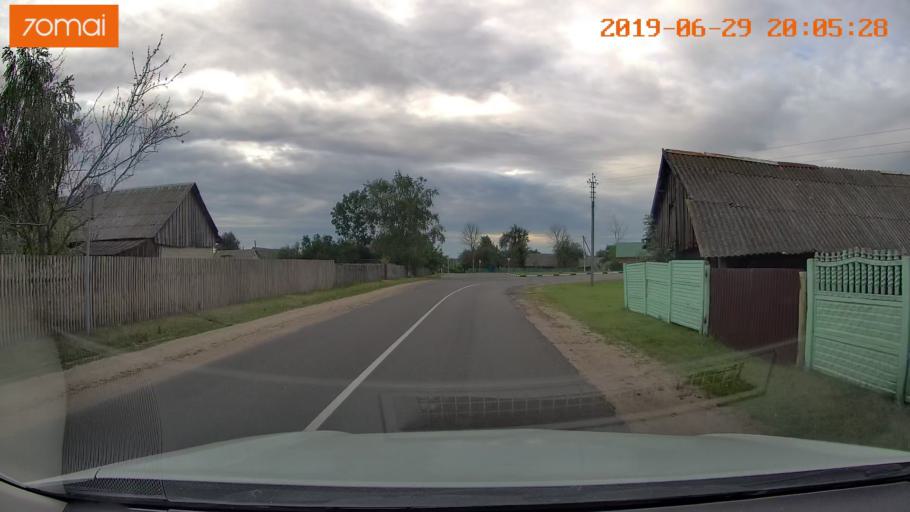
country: BY
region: Brest
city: Lahishyn
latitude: 52.3377
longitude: 26.0013
